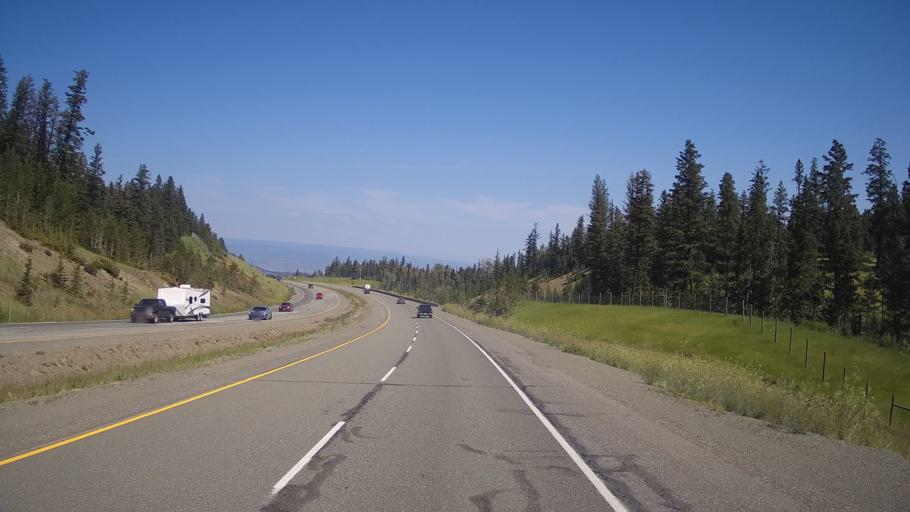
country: CA
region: British Columbia
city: Kamloops
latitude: 50.5557
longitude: -120.4491
